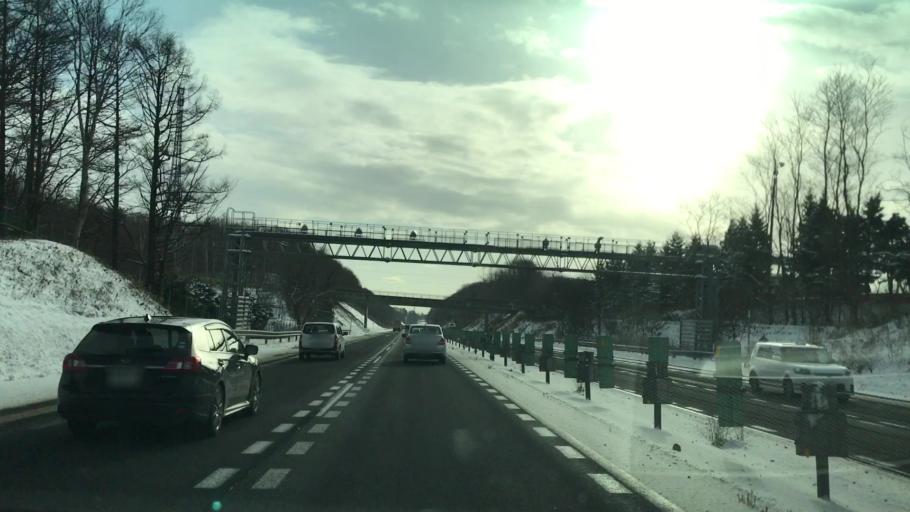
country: JP
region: Hokkaido
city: Kitahiroshima
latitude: 42.9336
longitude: 141.5286
